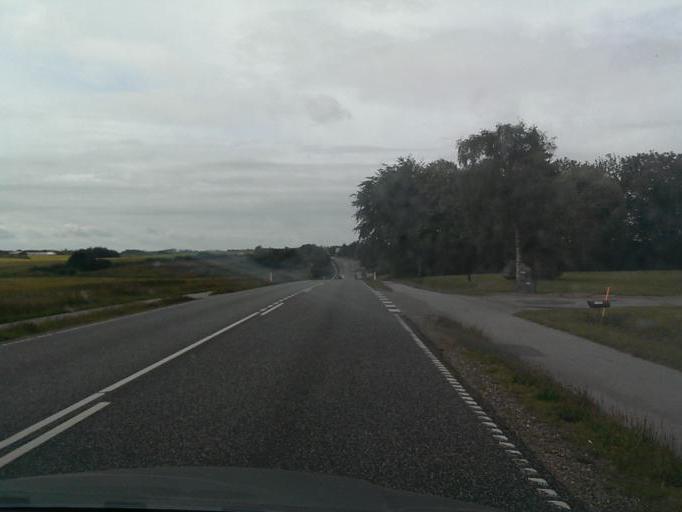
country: DK
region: North Denmark
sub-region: Hjorring Kommune
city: Hjorring
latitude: 57.4556
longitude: 9.9250
